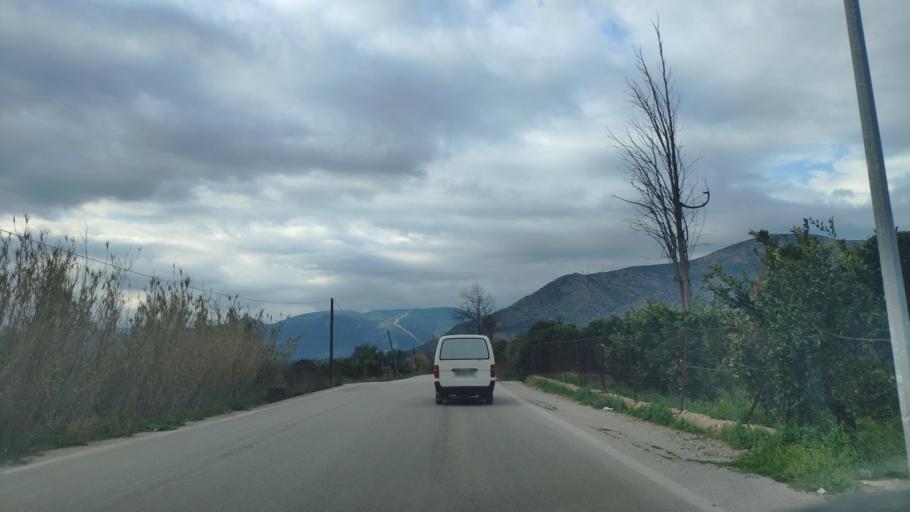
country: GR
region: Peloponnese
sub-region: Nomos Argolidos
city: Argos
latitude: 37.6127
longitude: 22.7055
